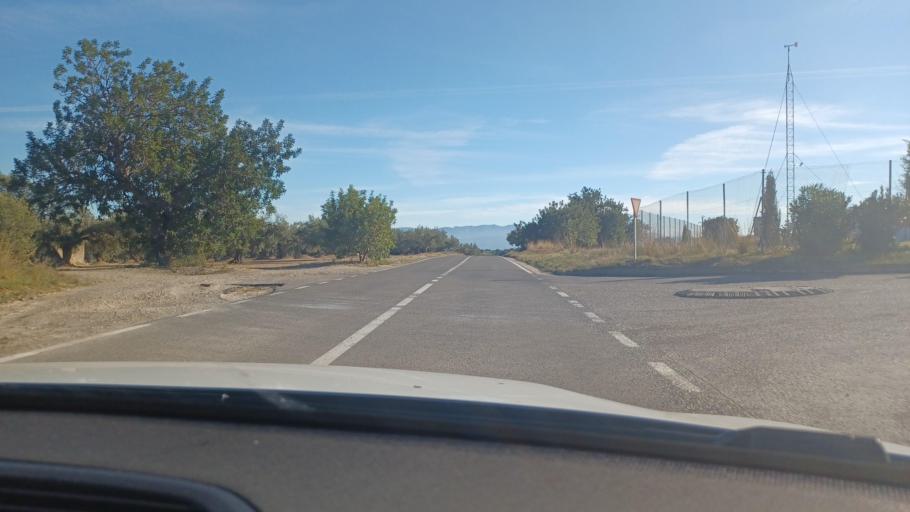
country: ES
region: Catalonia
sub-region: Provincia de Tarragona
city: Mas de Barberans
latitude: 40.7186
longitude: 0.3998
